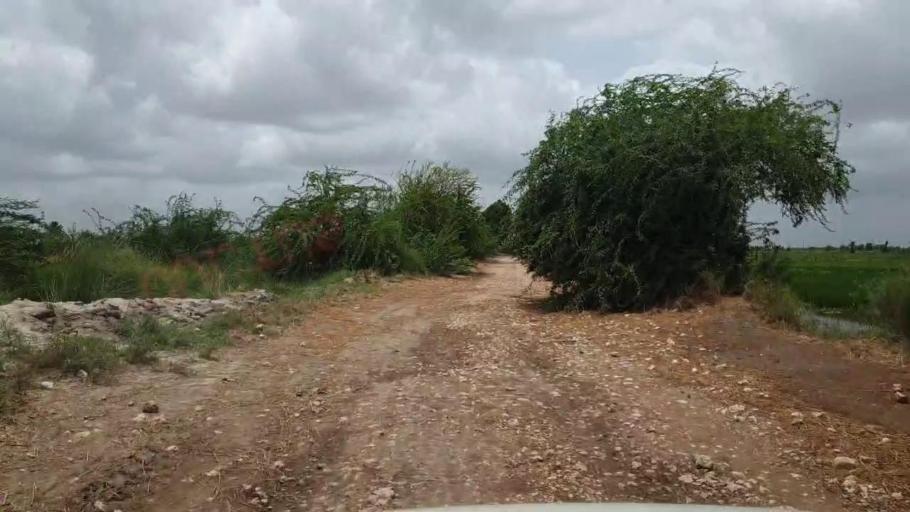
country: PK
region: Sindh
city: Kario
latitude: 24.7410
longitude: 68.5211
